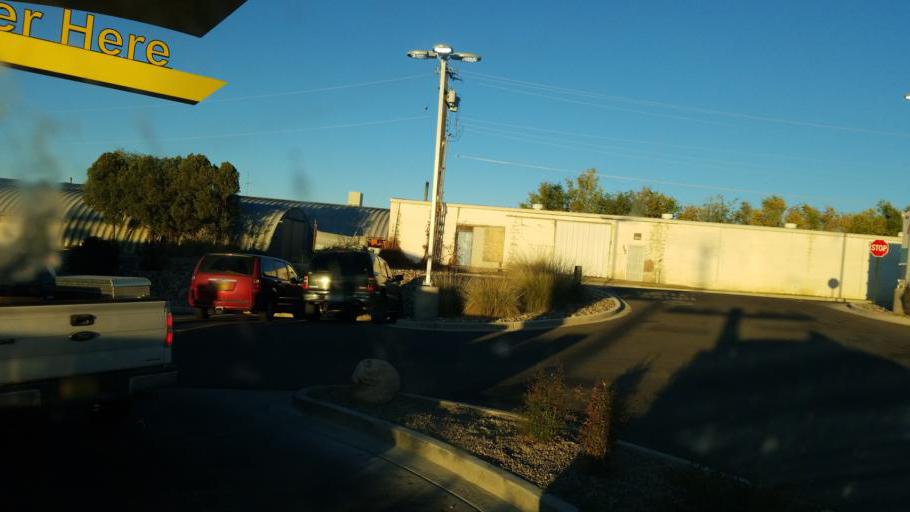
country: US
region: New Mexico
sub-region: San Juan County
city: Farmington
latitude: 36.7323
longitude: -108.2315
